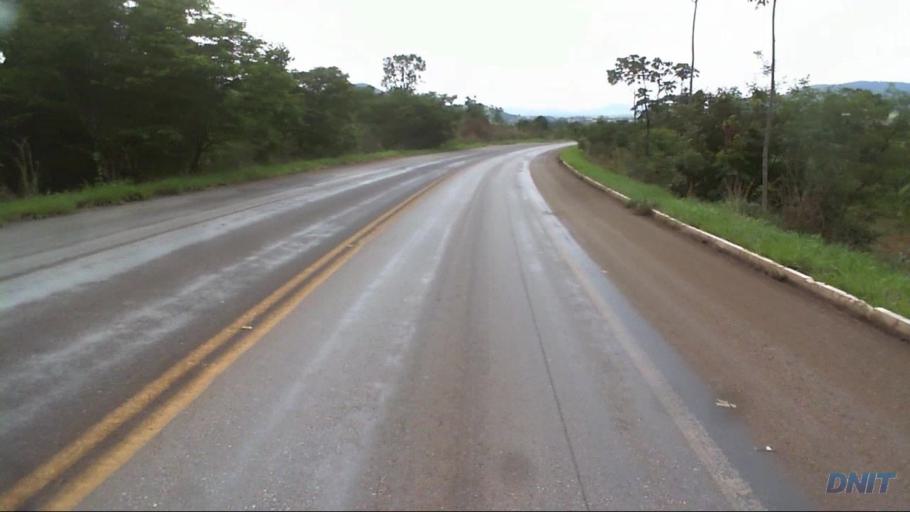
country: BR
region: Goias
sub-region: Barro Alto
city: Barro Alto
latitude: -14.9396
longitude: -48.9397
